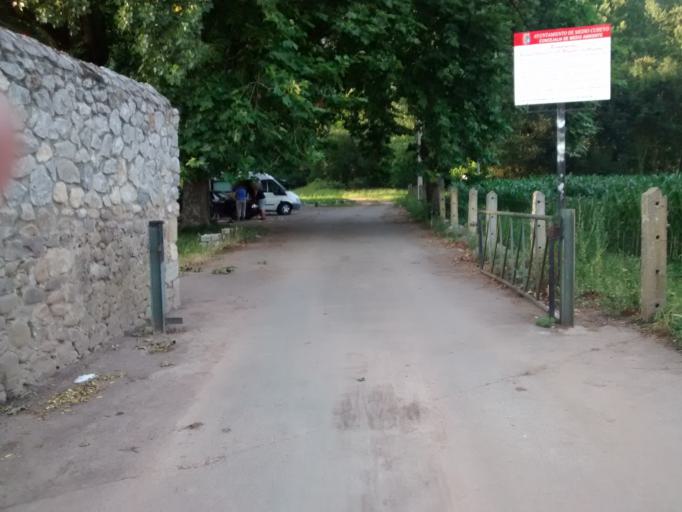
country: ES
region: Cantabria
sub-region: Provincia de Cantabria
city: Entrambasaguas
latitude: 43.3801
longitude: -3.7198
